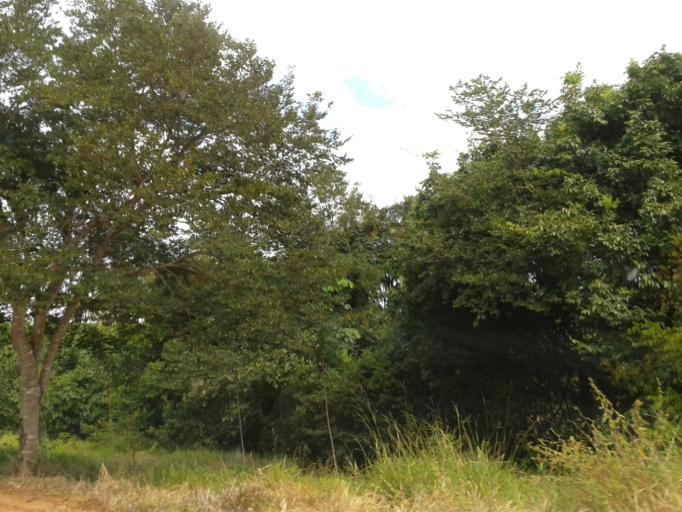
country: BR
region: Minas Gerais
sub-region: Campina Verde
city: Campina Verde
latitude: -19.3848
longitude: -49.6618
